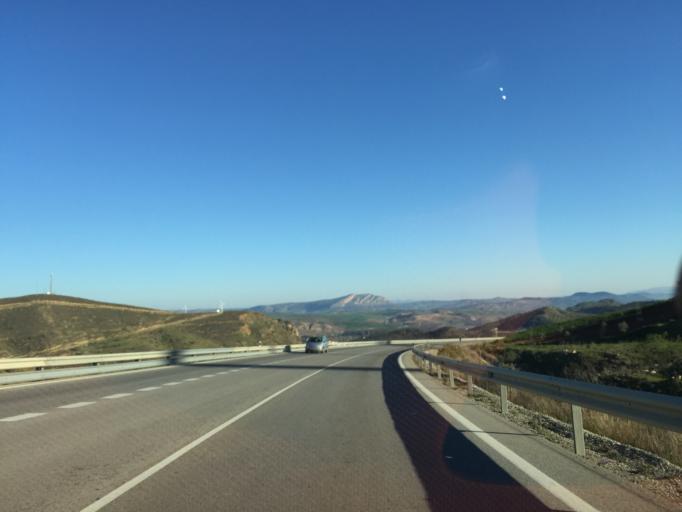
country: ES
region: Andalusia
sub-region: Provincia de Malaga
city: Ardales
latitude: 36.8656
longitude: -4.8423
